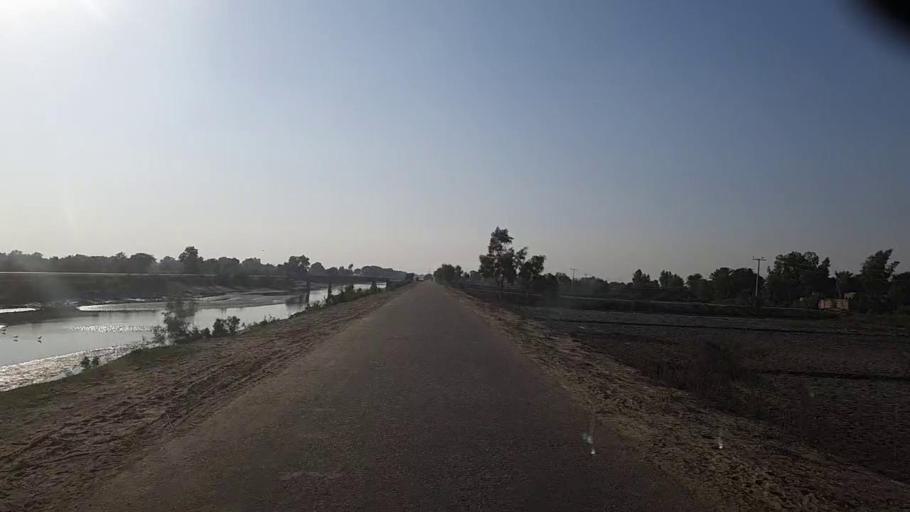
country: PK
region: Sindh
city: Tangwani
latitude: 28.3011
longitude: 68.9506
